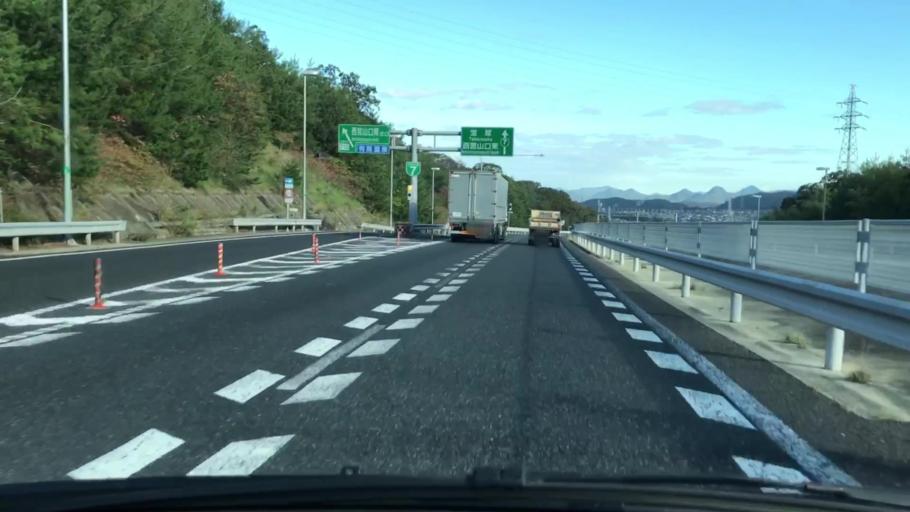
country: JP
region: Hyogo
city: Sandacho
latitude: 34.8135
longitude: 135.2471
